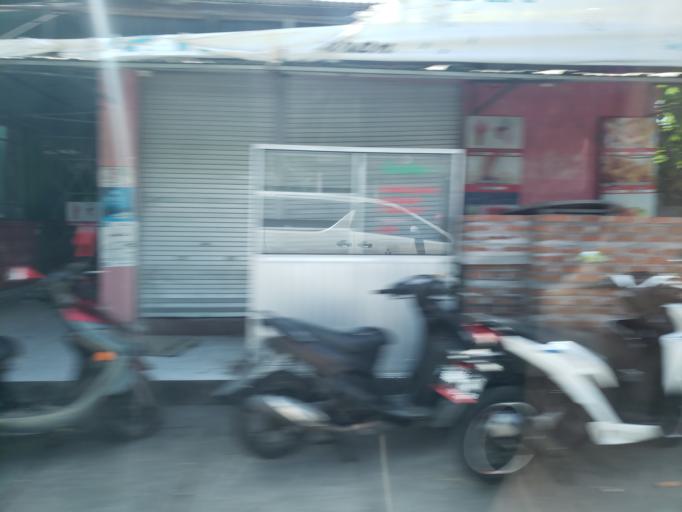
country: ID
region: Bali
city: Kangin
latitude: -8.8203
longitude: 115.1530
